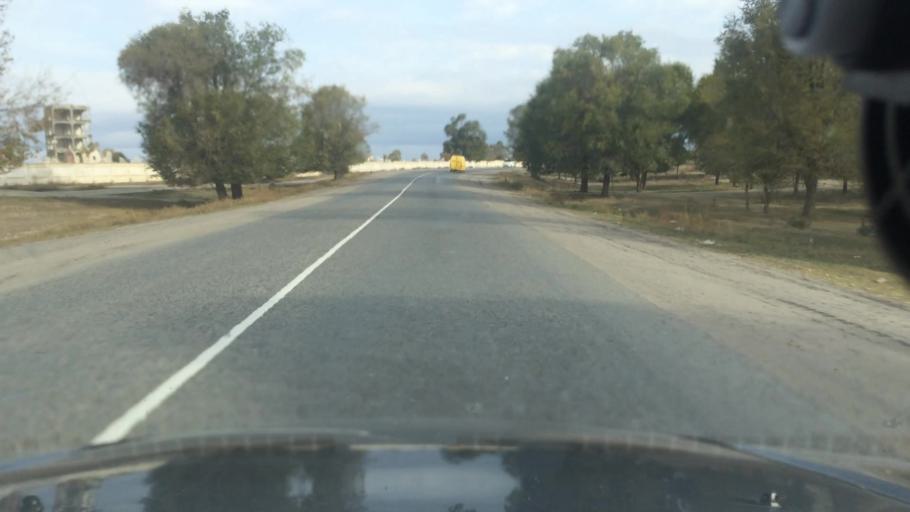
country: KG
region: Ysyk-Koel
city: Karakol
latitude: 42.5357
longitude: 78.3819
